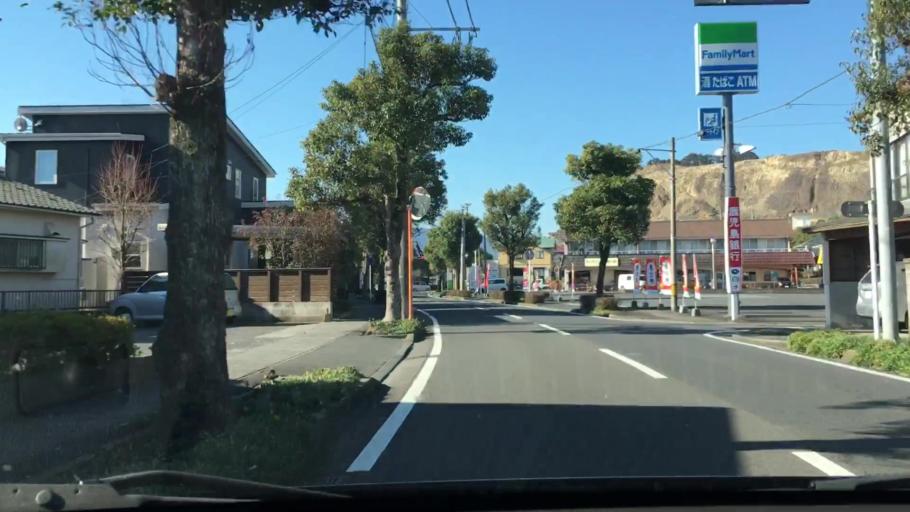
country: JP
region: Kagoshima
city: Kajiki
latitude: 31.7399
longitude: 130.6551
